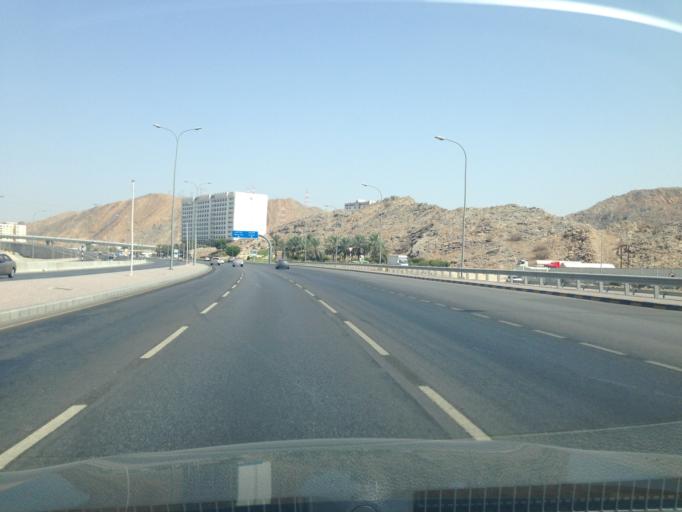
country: OM
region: Muhafazat Masqat
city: Muscat
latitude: 23.5958
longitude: 58.5210
